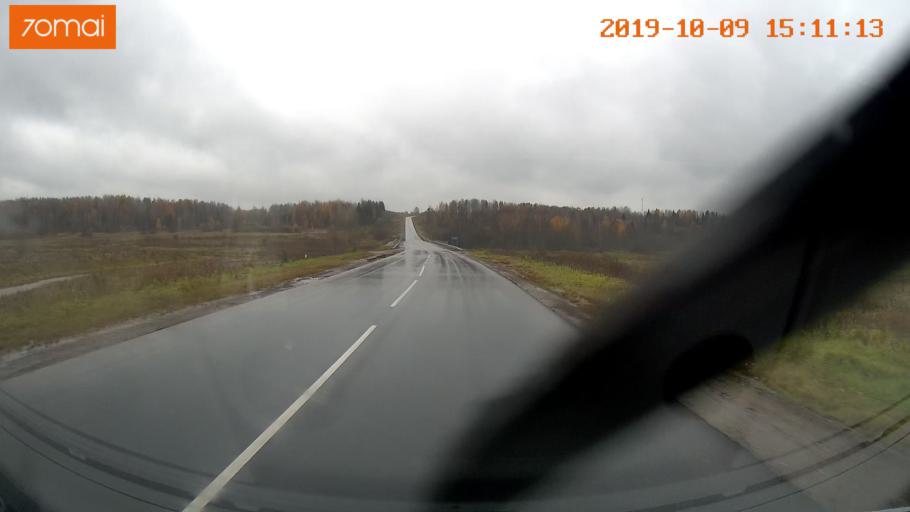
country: RU
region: Kostroma
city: Susanino
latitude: 58.1679
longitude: 41.6312
